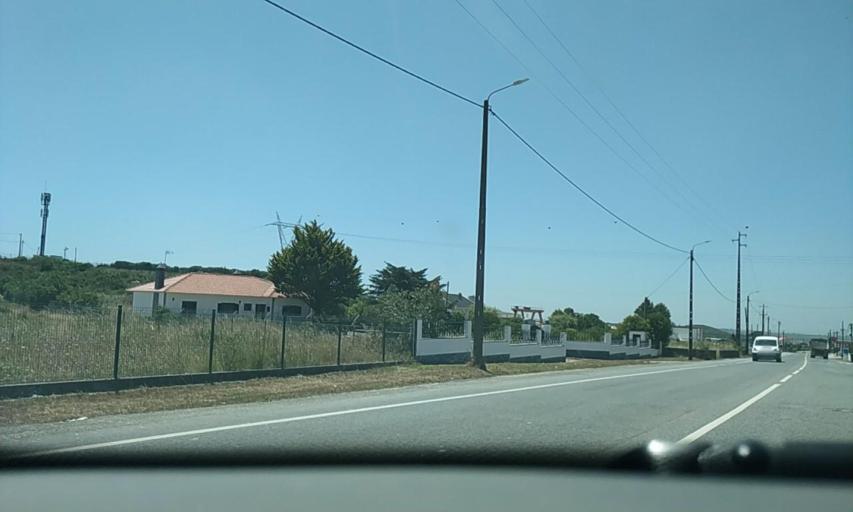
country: PT
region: Lisbon
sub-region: Sintra
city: Almargem
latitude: 38.8769
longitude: -9.2655
